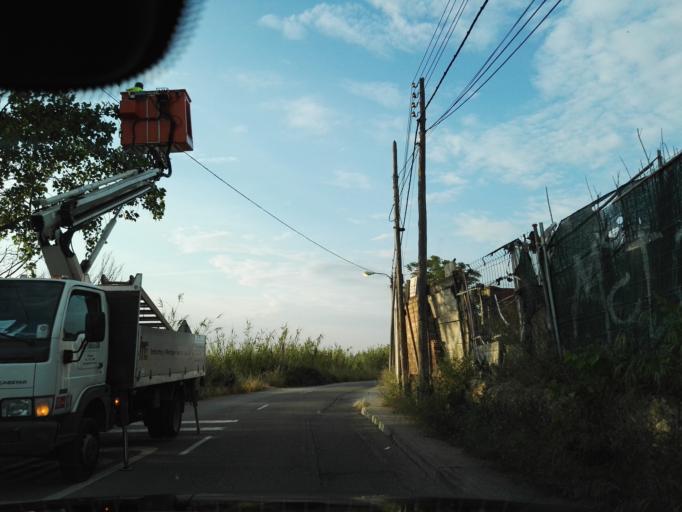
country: ES
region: Aragon
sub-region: Provincia de Zaragoza
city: Zaragoza
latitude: 41.6322
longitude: -0.8707
